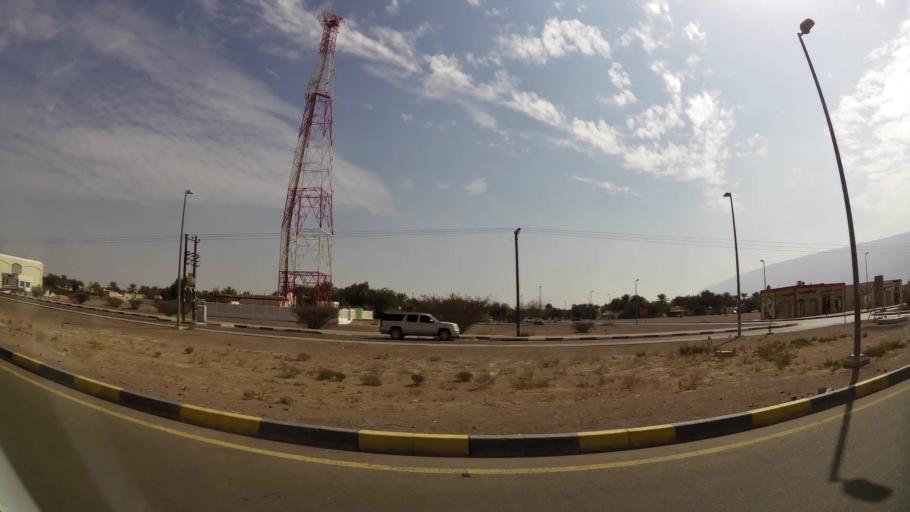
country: AE
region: Abu Dhabi
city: Al Ain
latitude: 24.0862
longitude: 55.8356
